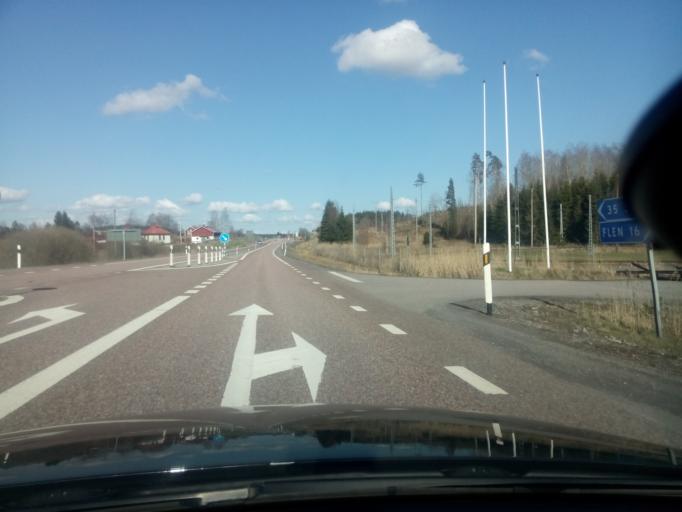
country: SE
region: Soedermanland
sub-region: Flens Kommun
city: Malmkoping
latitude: 59.1556
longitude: 16.7313
